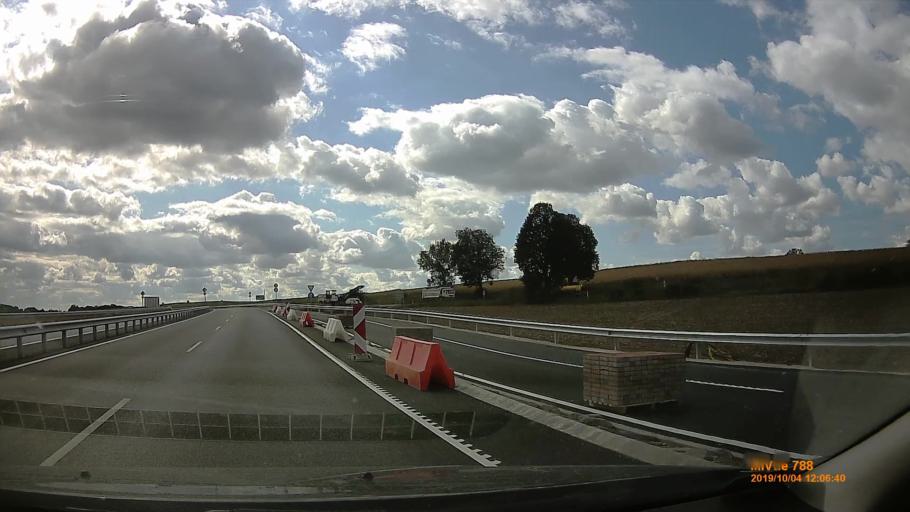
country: HU
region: Somogy
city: Karad
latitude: 46.5501
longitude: 17.8140
